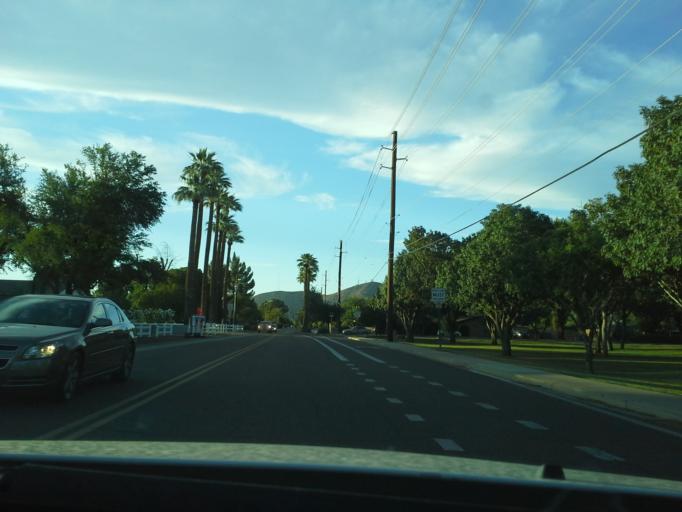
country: US
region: Arizona
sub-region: Maricopa County
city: Glendale
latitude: 33.5593
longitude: -112.0912
